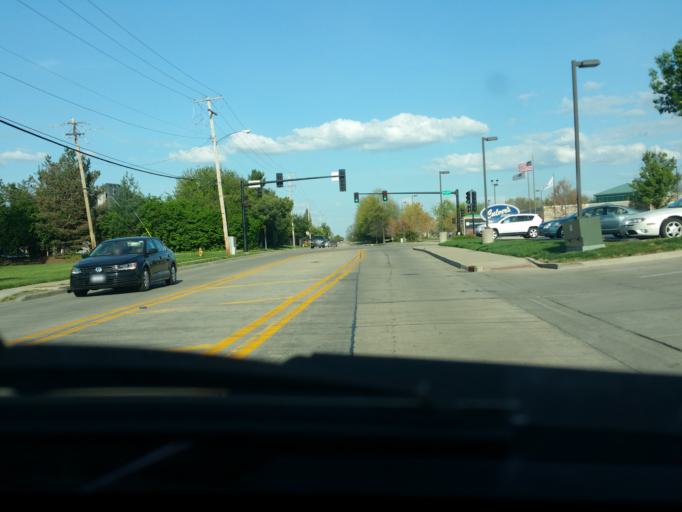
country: US
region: Illinois
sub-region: Madison County
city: Edwardsville
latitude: 38.7813
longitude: -89.9486
